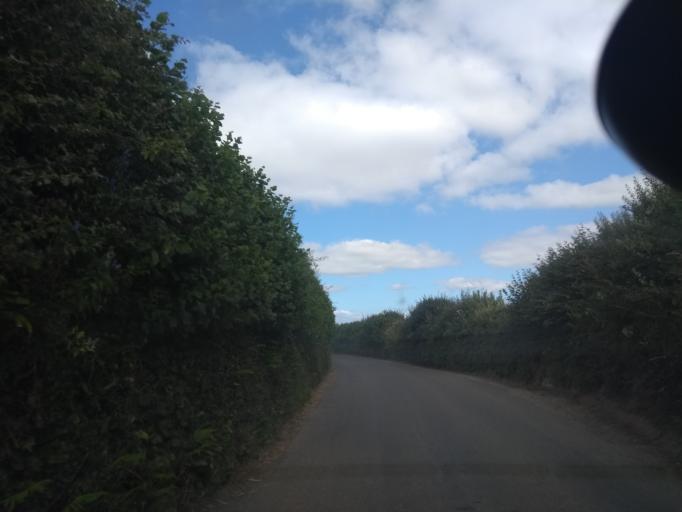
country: GB
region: England
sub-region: Devon
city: Modbury
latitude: 50.3093
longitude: -3.8807
